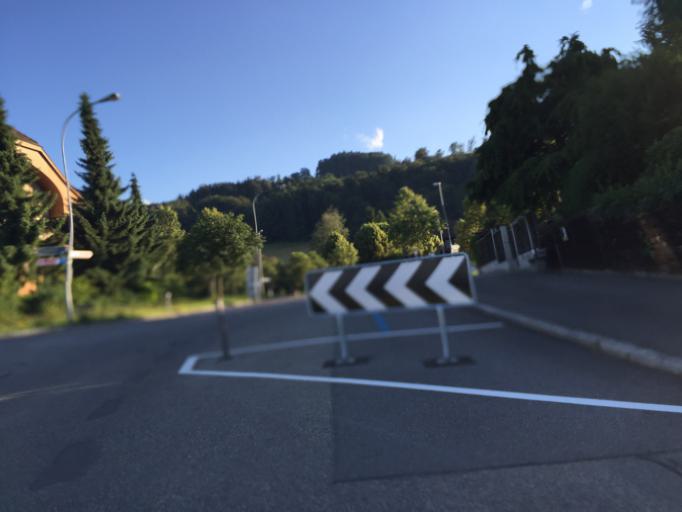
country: CH
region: Bern
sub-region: Bern-Mittelland District
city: Kehrsatz
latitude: 46.9234
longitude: 7.4615
